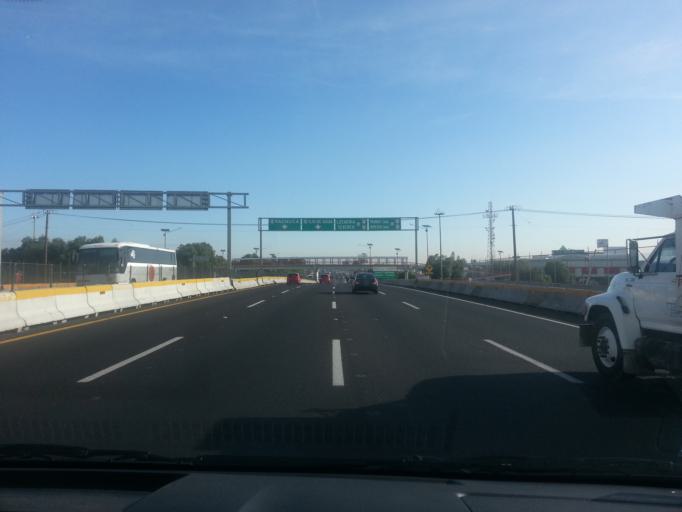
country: MX
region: Mexico
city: Ecatepec
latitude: 19.5892
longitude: -99.0416
